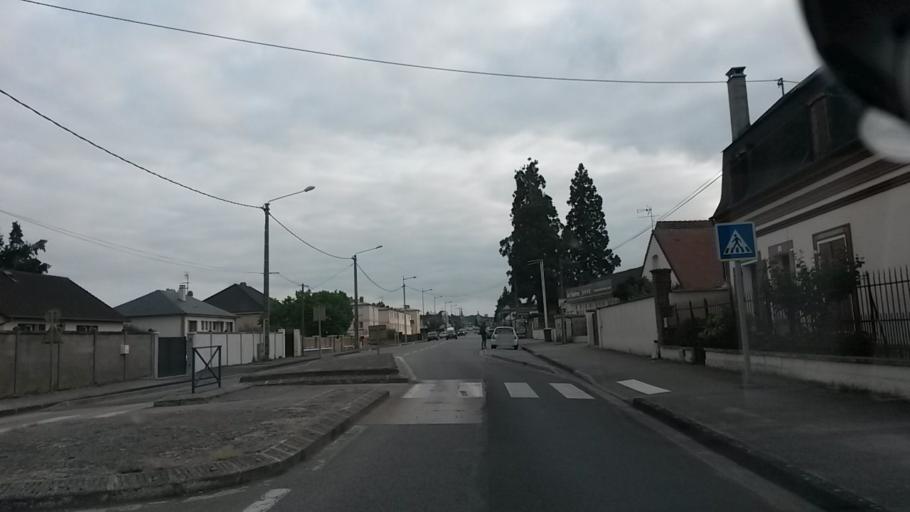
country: FR
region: Haute-Normandie
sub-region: Departement de l'Eure
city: Gravigny
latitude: 49.0413
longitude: 1.1590
